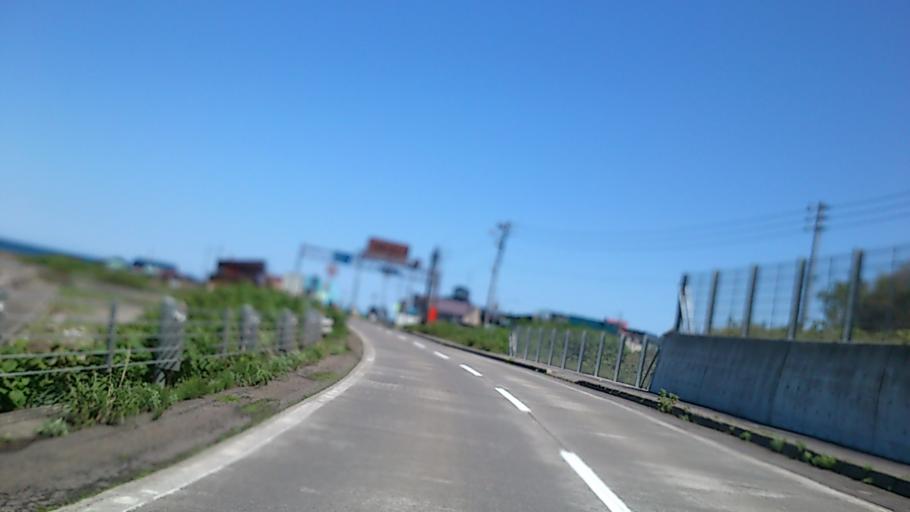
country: JP
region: Hokkaido
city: Rumoi
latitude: 43.7348
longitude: 141.3385
